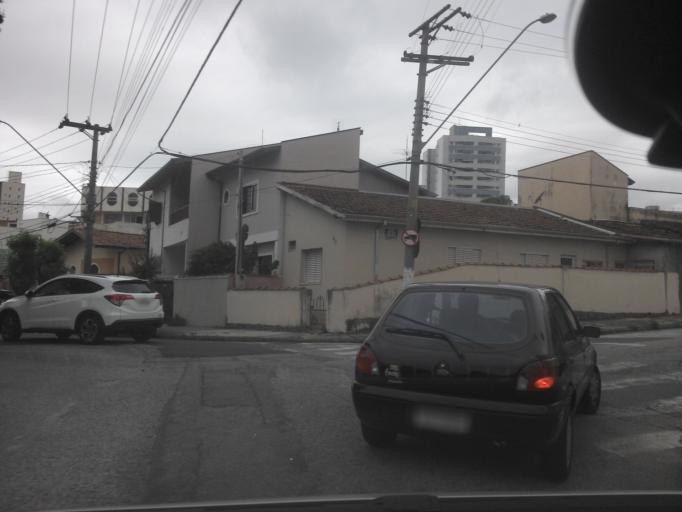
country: BR
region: Sao Paulo
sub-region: Taubate
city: Taubate
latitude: -23.0362
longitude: -45.5637
